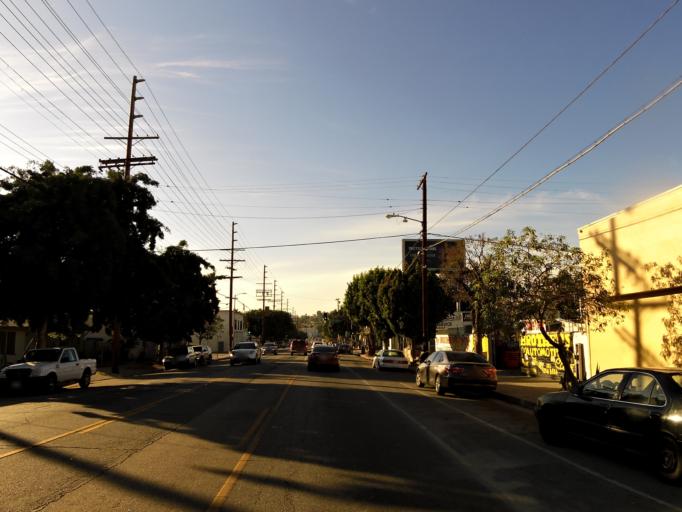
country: US
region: California
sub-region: Los Angeles County
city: Glendale
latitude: 34.1231
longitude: -118.2154
